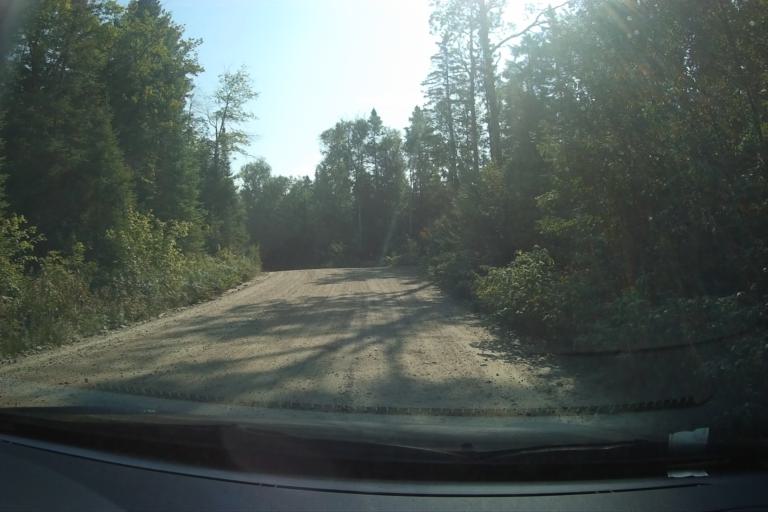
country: CA
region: Ontario
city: Huntsville
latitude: 45.5640
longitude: -78.7020
